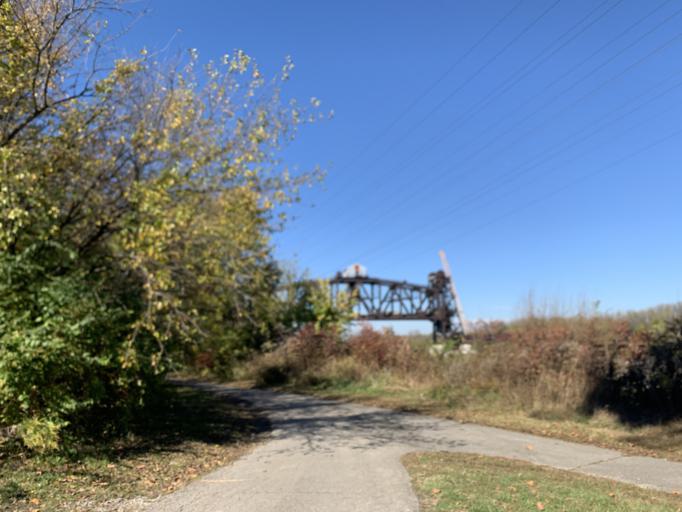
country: US
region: Kentucky
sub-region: Jefferson County
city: Louisville
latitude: 38.2617
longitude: -85.7702
